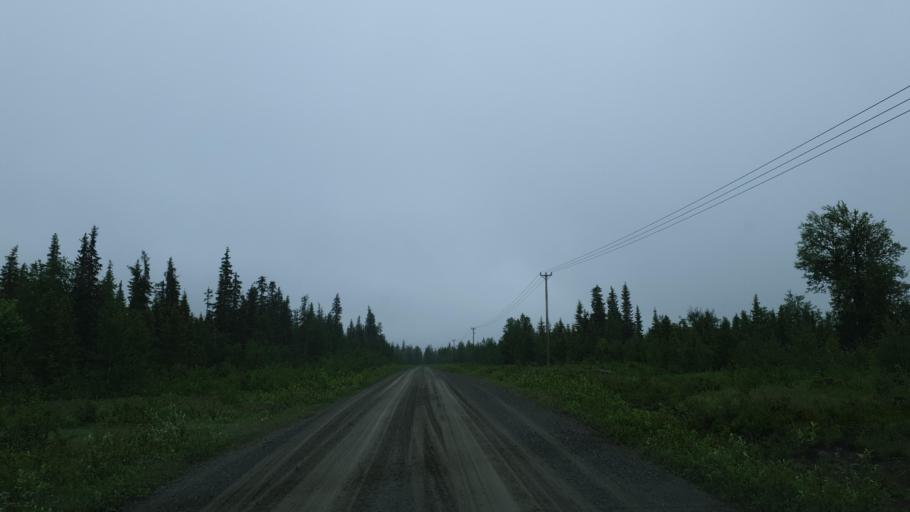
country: SE
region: Vaesterbotten
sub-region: Vilhelmina Kommun
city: Sjoberg
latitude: 65.3129
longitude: 15.9647
